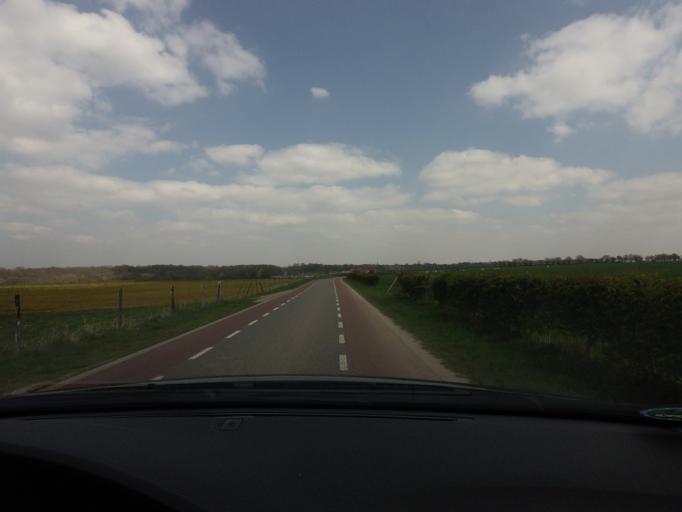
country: NL
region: Limburg
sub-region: Eijsden-Margraten
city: Eijsden
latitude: 50.7798
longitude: 5.7559
